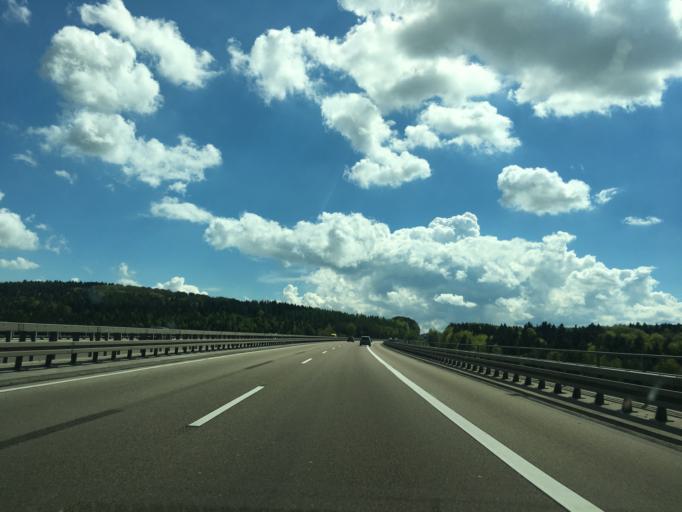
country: DE
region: Bavaria
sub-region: Regierungsbezirk Unterfranken
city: Motten
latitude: 50.4323
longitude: 9.7438
